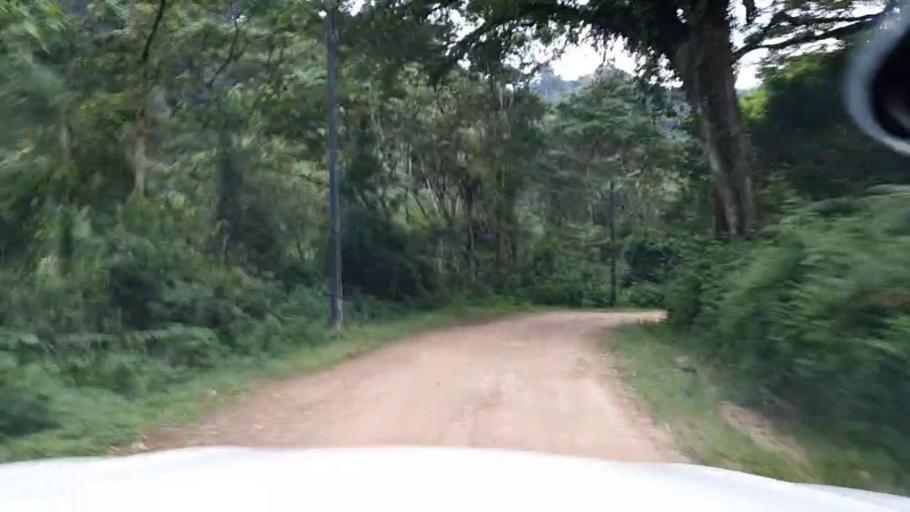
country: RW
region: Western Province
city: Cyangugu
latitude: -2.5698
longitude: 29.2244
